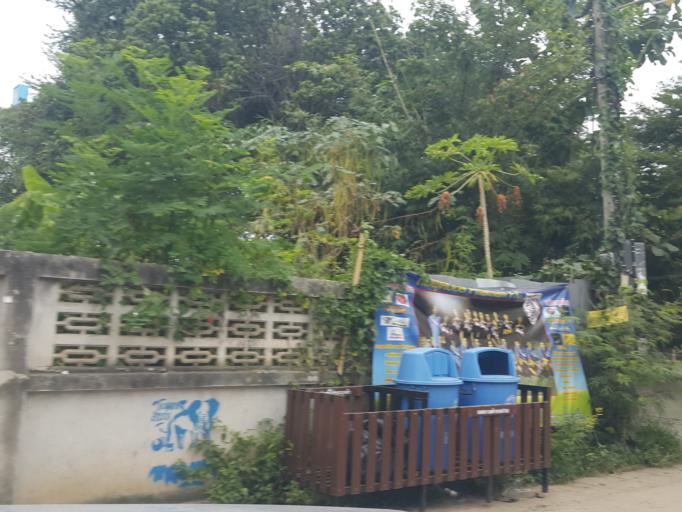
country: TH
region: Chiang Mai
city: Pai
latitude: 19.3589
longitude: 98.4420
